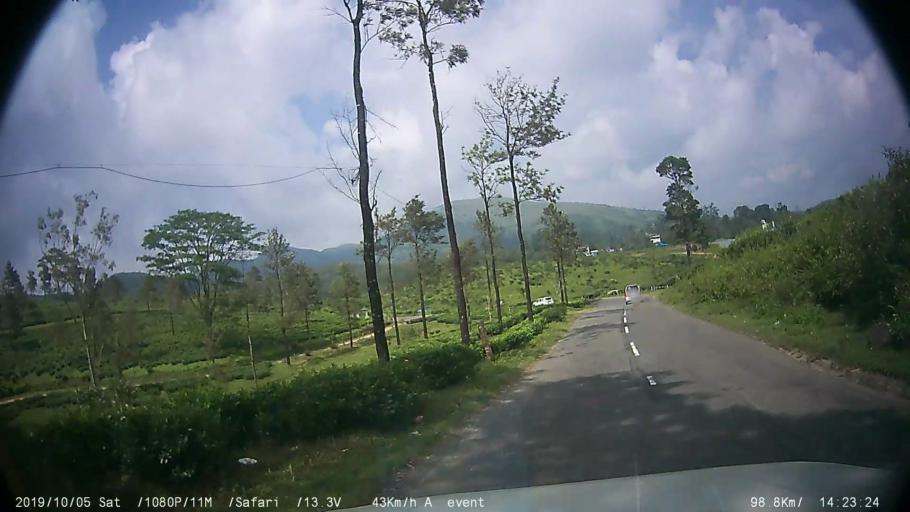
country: IN
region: Kerala
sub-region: Kottayam
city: Erattupetta
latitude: 9.5905
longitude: 76.9680
